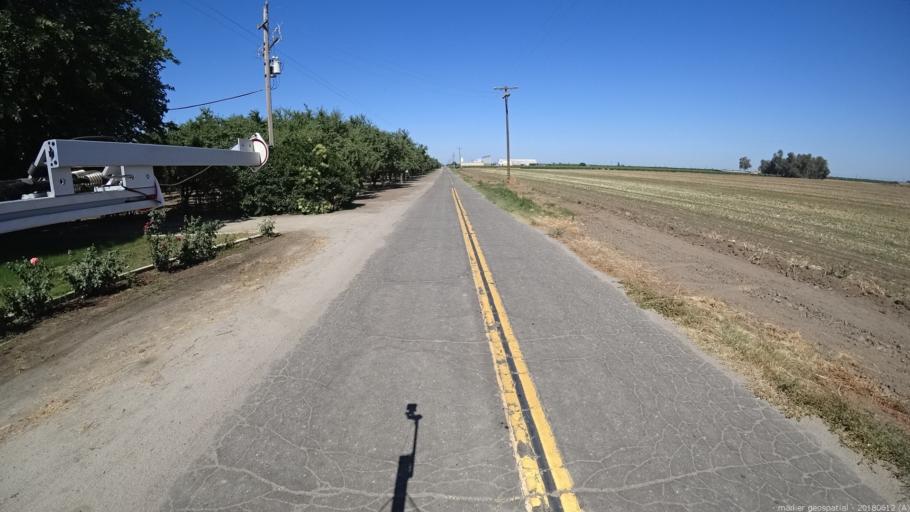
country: US
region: California
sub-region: Madera County
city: Chowchilla
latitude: 37.0327
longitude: -120.3032
